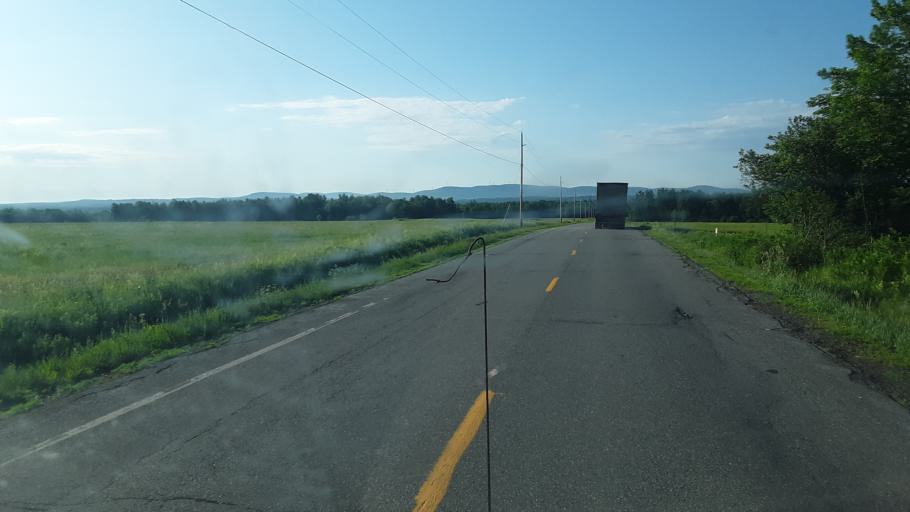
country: US
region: Maine
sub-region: Penobscot County
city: Patten
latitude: 46.1696
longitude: -68.2359
